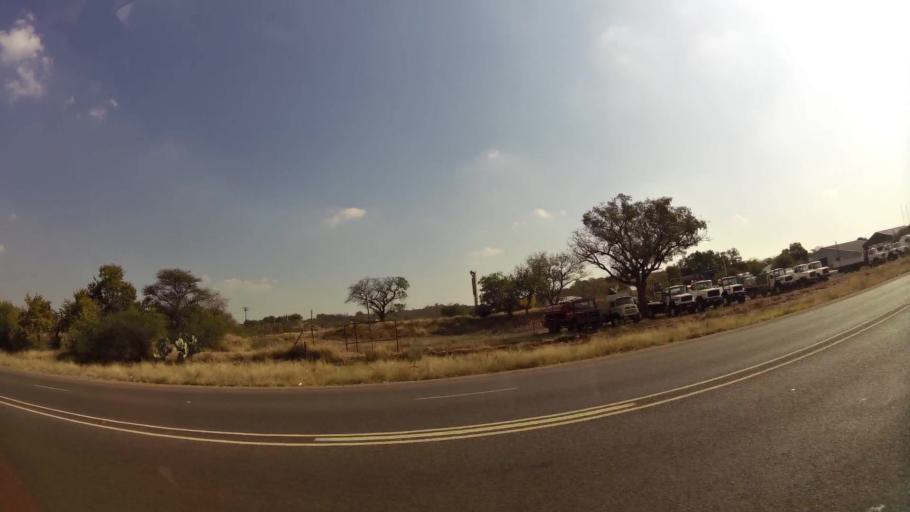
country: ZA
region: North-West
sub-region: Bojanala Platinum District Municipality
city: Mogwase
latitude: -25.4481
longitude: 27.0881
